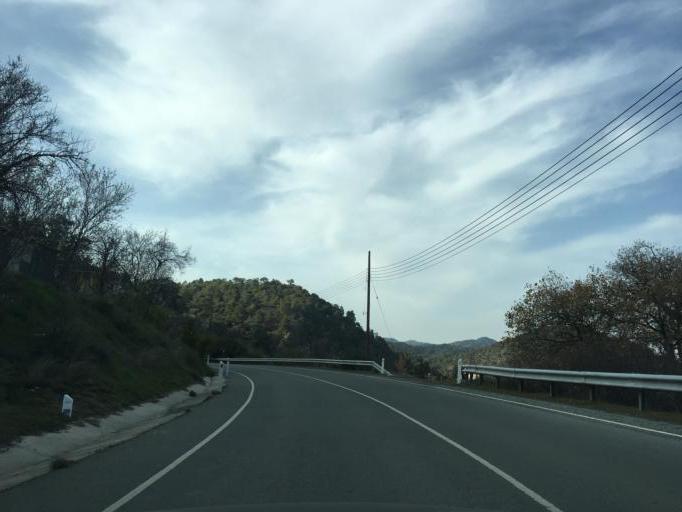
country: CY
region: Limassol
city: Pelendri
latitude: 34.8217
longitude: 32.9652
